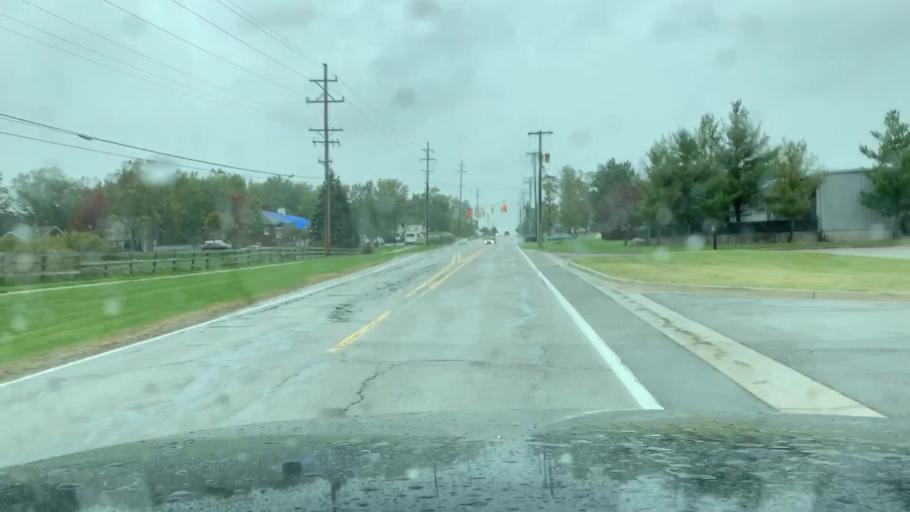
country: US
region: Michigan
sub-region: Ottawa County
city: Zeeland
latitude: 42.7822
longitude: -86.0577
